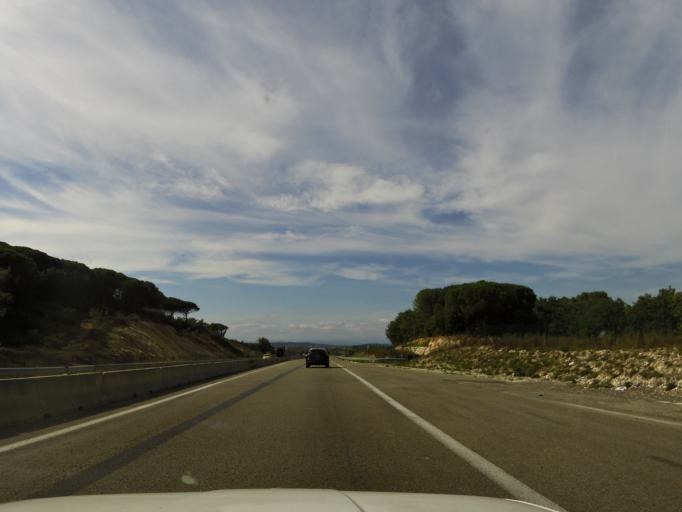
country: FR
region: Languedoc-Roussillon
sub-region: Departement du Gard
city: La Calmette
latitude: 43.9136
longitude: 4.2658
